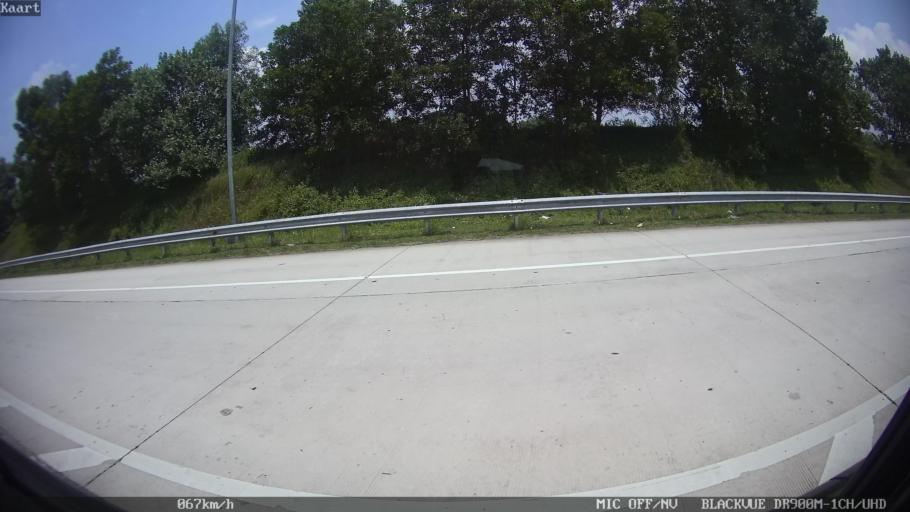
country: ID
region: Lampung
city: Natar
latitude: -5.2789
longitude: 105.2166
